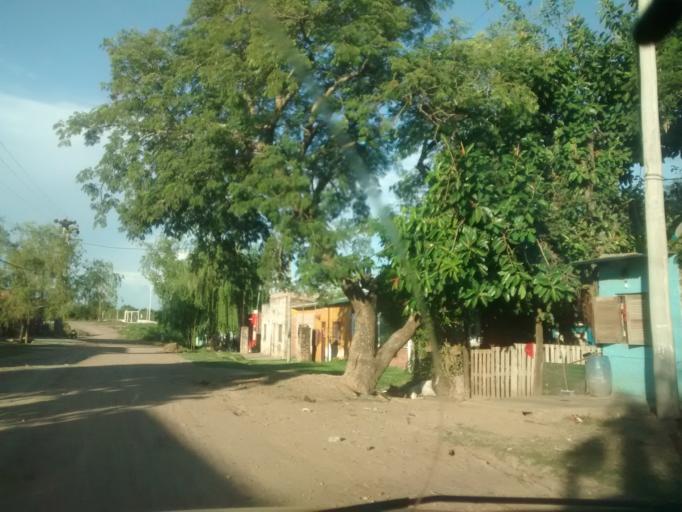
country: AR
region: Chaco
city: Resistencia
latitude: -27.4304
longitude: -58.9919
